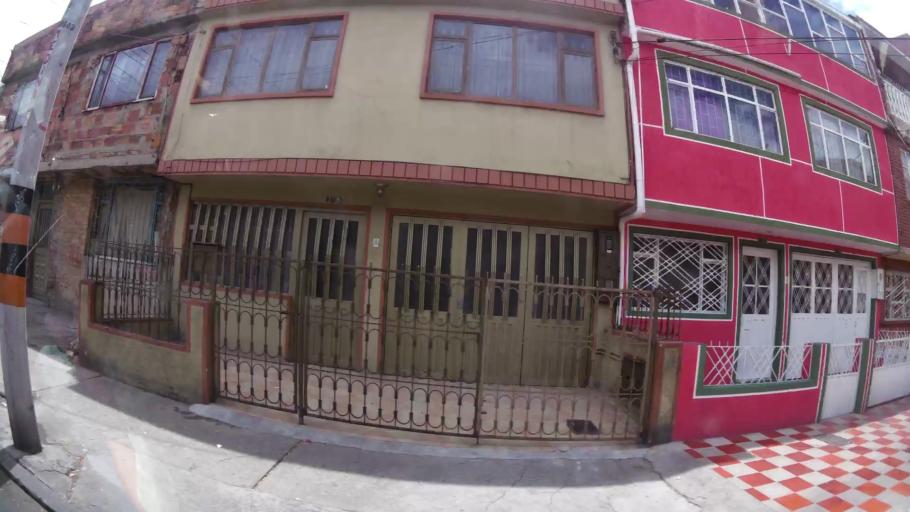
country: CO
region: Bogota D.C.
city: Bogota
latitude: 4.6110
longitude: -74.1125
